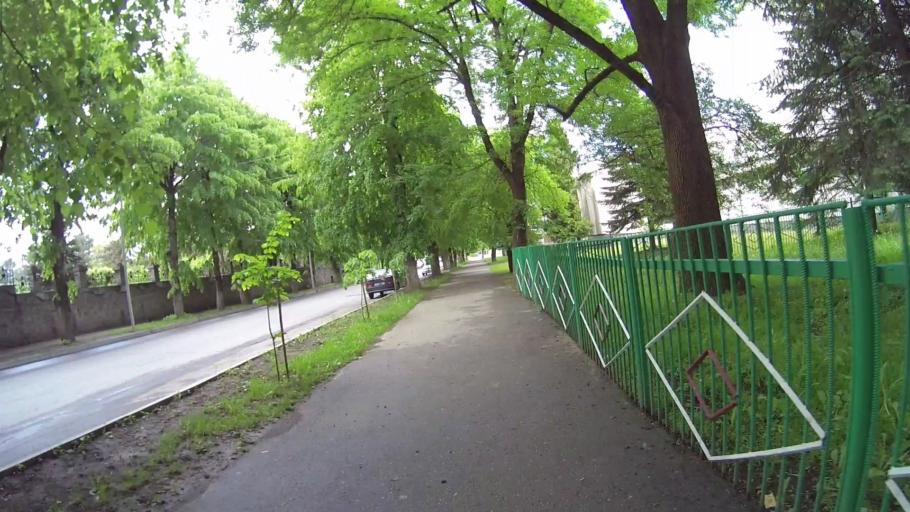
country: RU
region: Kabardino-Balkariya
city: Vol'nyy Aul
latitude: 43.4688
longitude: 43.5855
